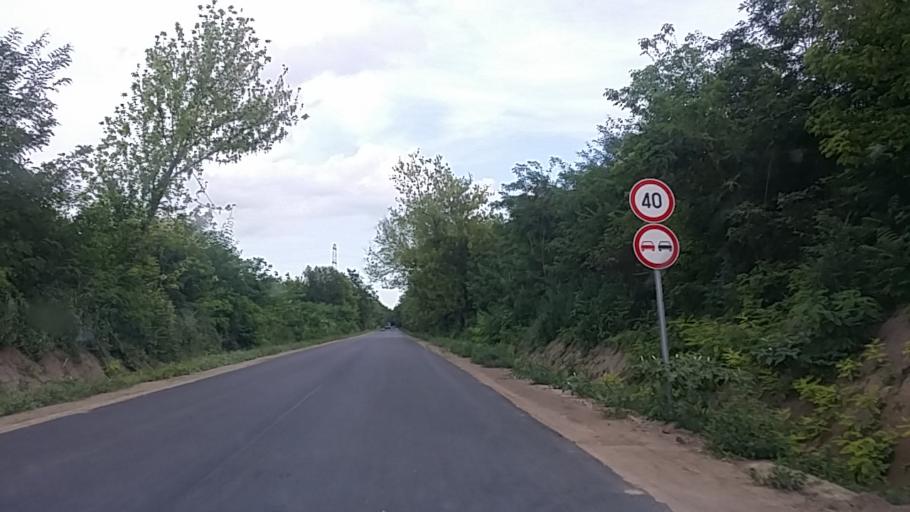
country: HU
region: Tolna
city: Tengelic
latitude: 46.5520
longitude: 18.7314
